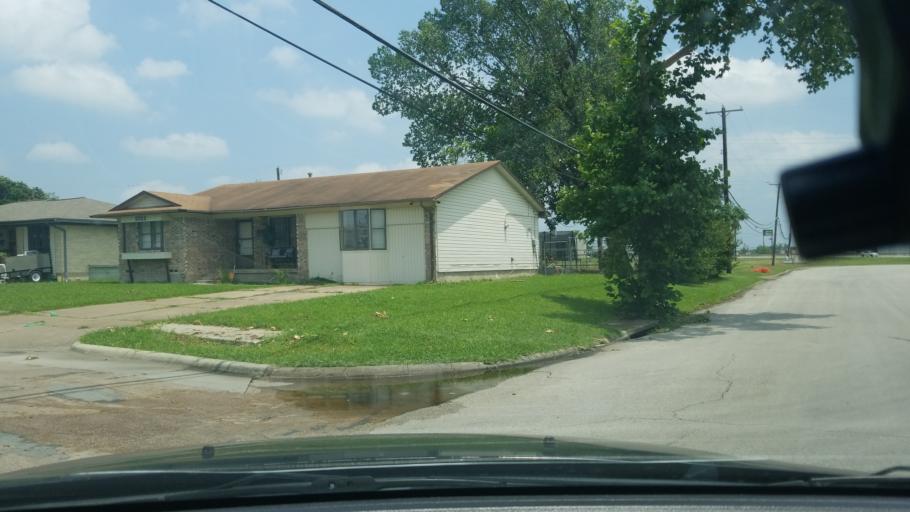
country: US
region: Texas
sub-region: Dallas County
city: Mesquite
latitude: 32.7939
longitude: -96.6391
